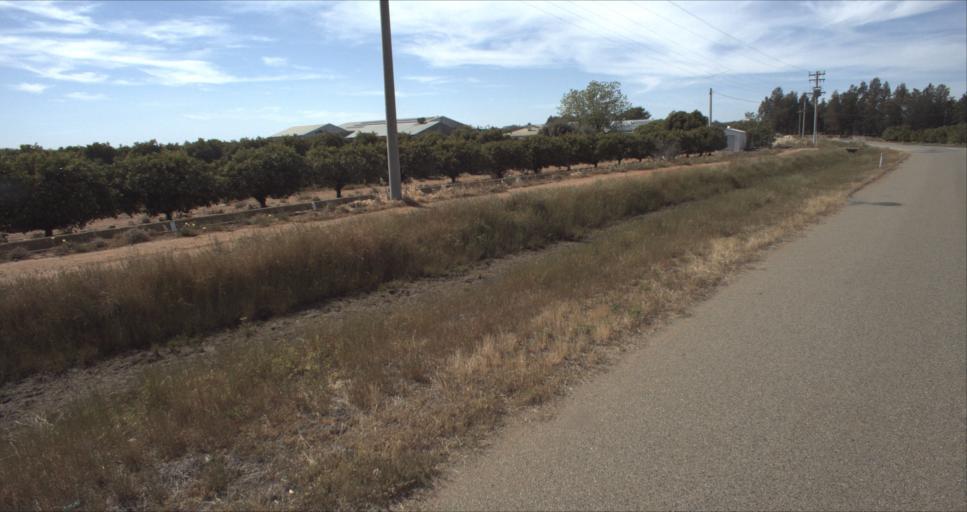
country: AU
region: New South Wales
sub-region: Leeton
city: Leeton
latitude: -34.5895
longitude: 146.4622
